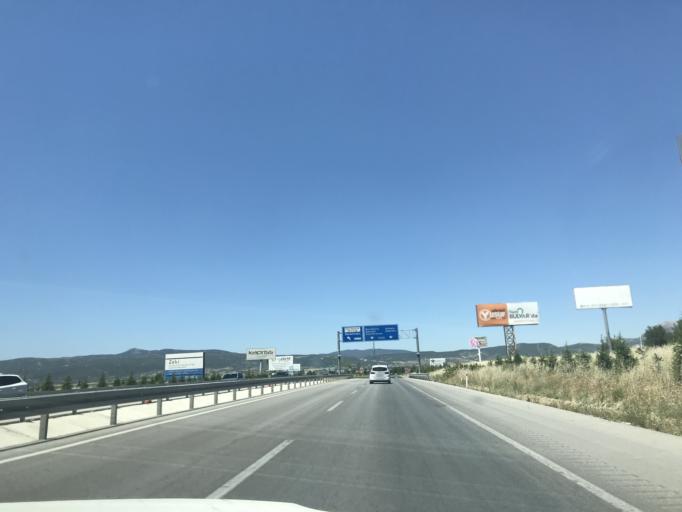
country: TR
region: Isparta
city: Keciborlu
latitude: 37.8964
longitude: 30.3894
